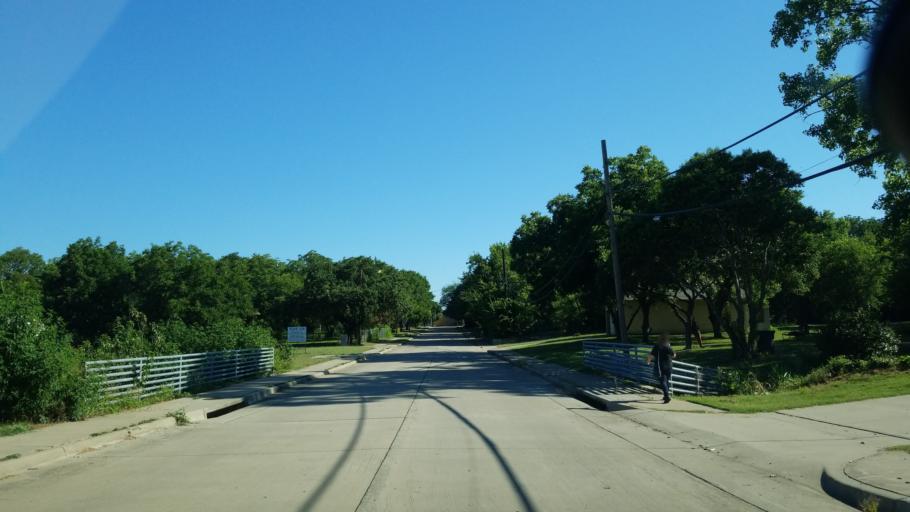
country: US
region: Texas
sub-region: Dallas County
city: Carrollton
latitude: 32.9508
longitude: -96.8974
